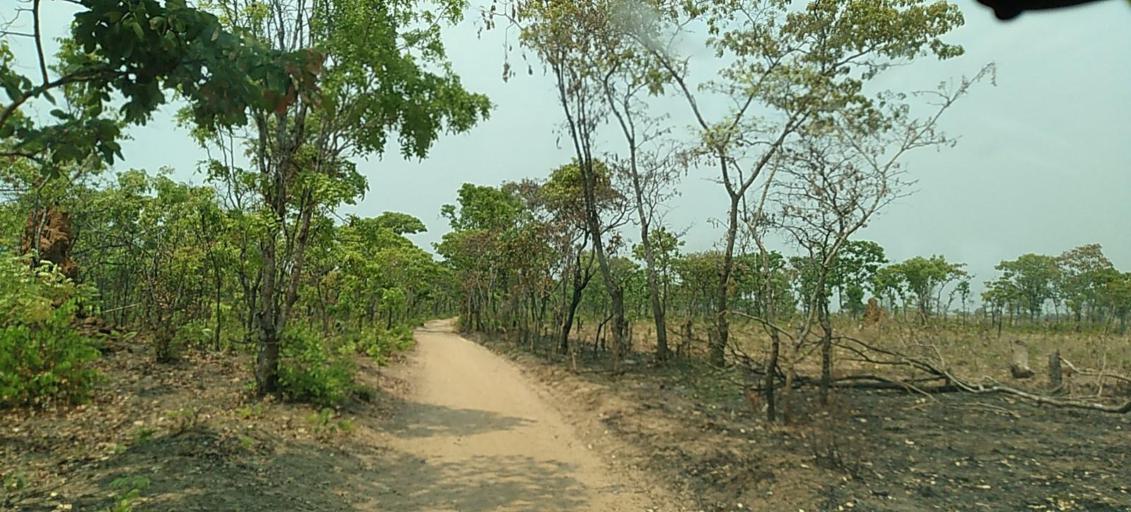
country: ZM
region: North-Western
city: Kabompo
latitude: -13.5260
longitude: 24.4641
